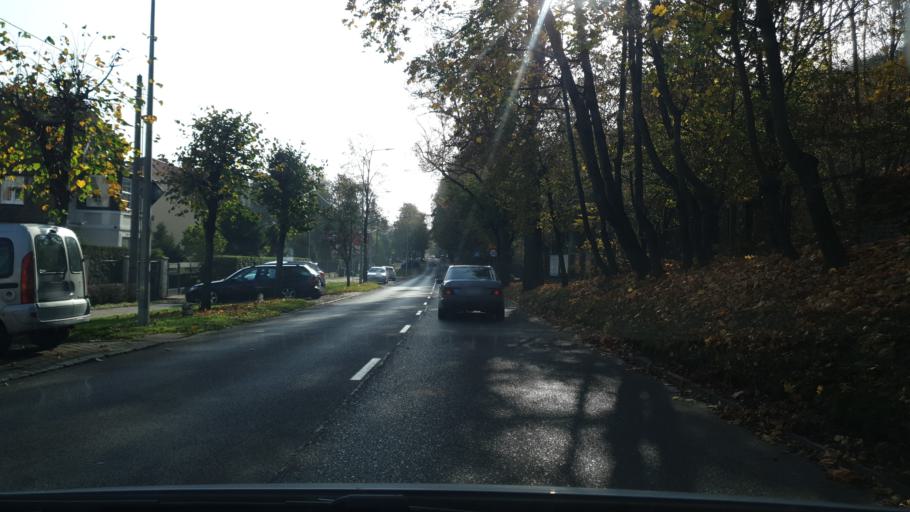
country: PL
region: Pomeranian Voivodeship
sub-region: Sopot
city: Sopot
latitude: 54.4024
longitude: 18.5612
